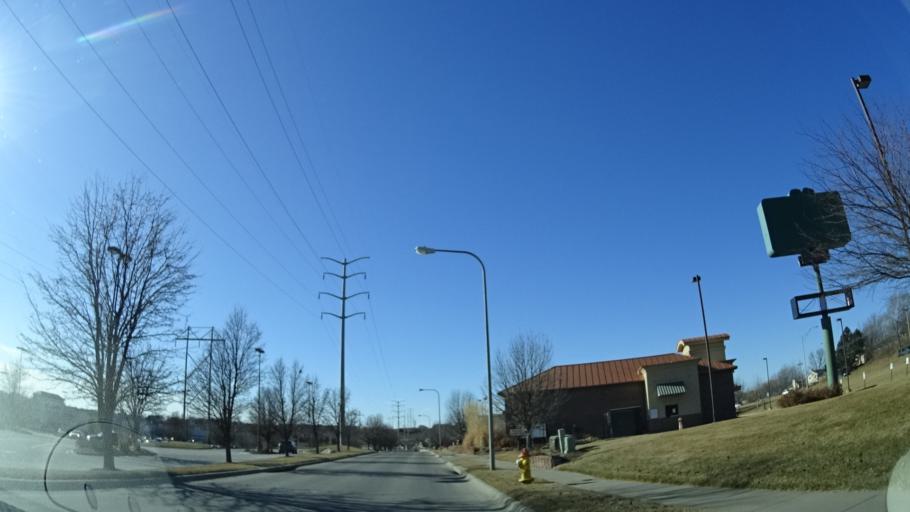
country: US
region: Nebraska
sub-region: Sarpy County
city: Offutt Air Force Base
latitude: 41.1576
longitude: -95.9318
